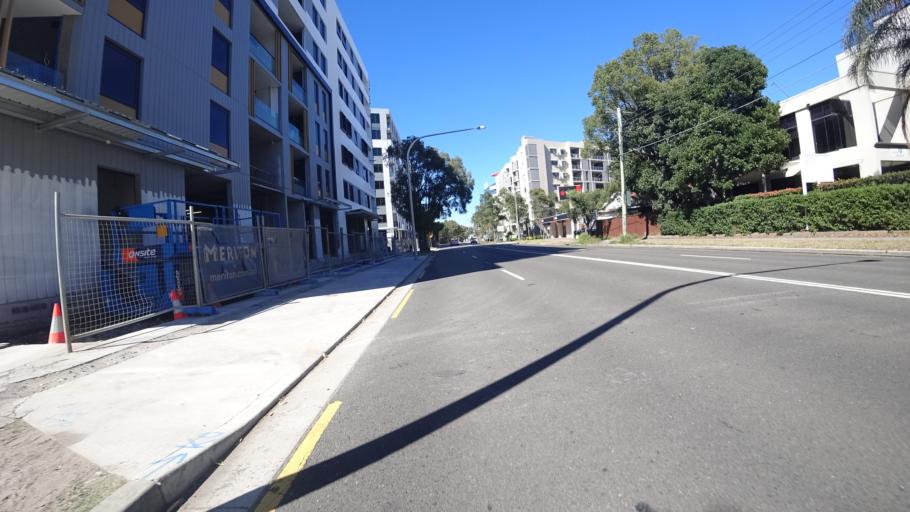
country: AU
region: New South Wales
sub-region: Botany Bay
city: Mascot
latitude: -33.9237
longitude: 151.1911
